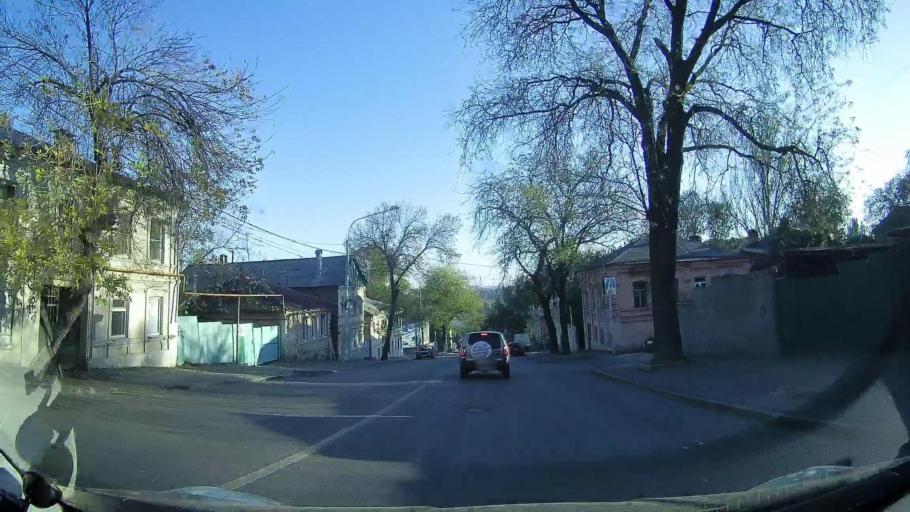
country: RU
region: Rostov
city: Rostov-na-Donu
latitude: 47.2214
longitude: 39.7323
